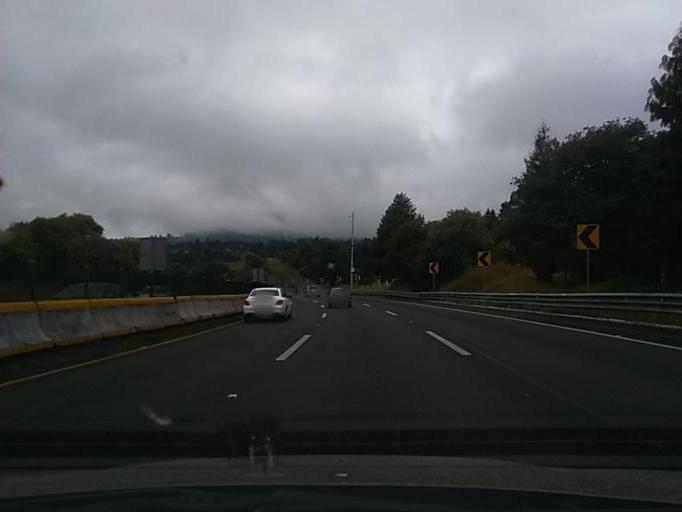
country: MX
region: Mexico City
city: Xochimilco
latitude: 19.1939
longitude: -99.1574
